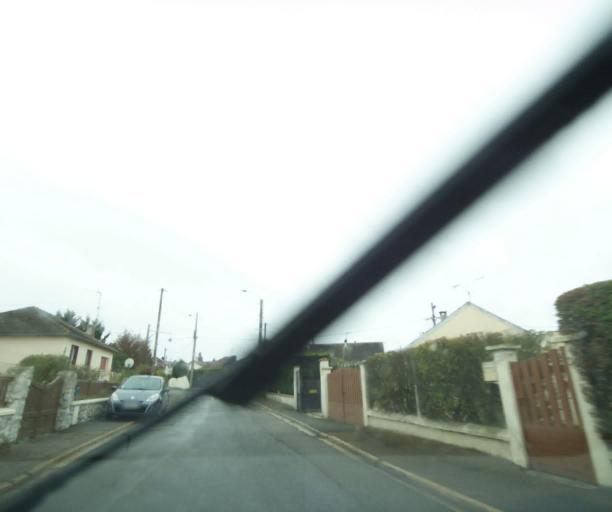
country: FR
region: Centre
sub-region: Departement d'Eure-et-Loir
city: Vernouillet
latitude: 48.7205
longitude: 1.3619
